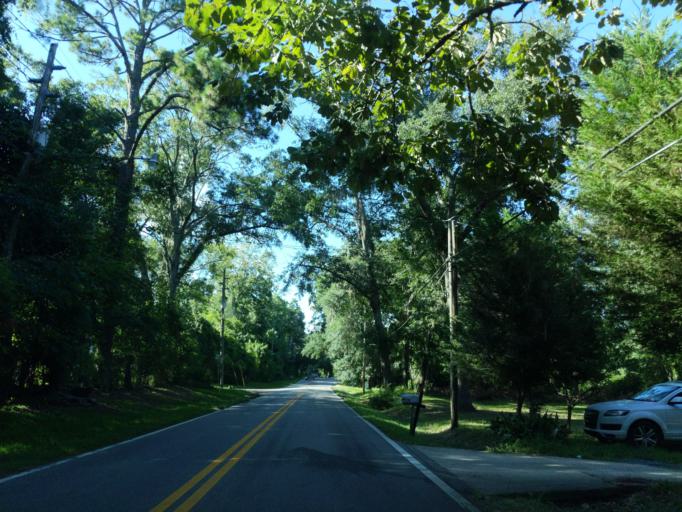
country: US
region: Florida
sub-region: Leon County
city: Tallahassee
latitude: 30.4177
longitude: -84.2436
